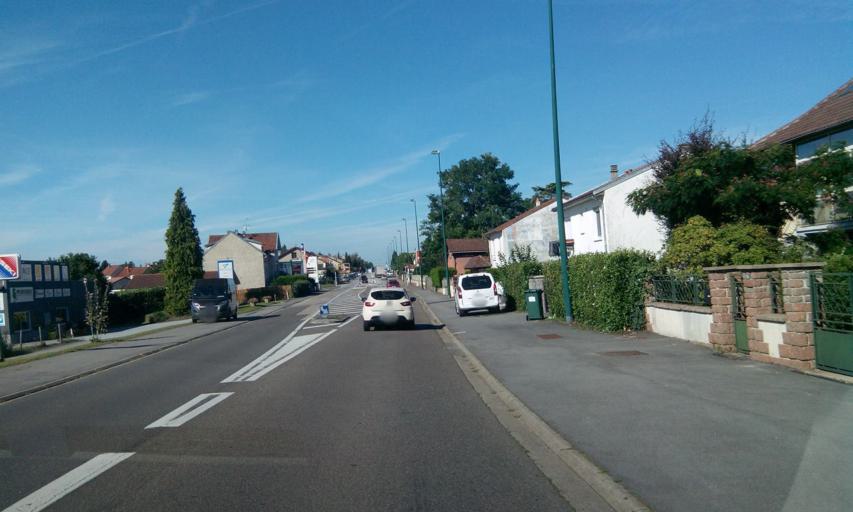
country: FR
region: Limousin
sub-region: Departement de la Haute-Vienne
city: Panazol
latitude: 45.8331
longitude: 1.3055
